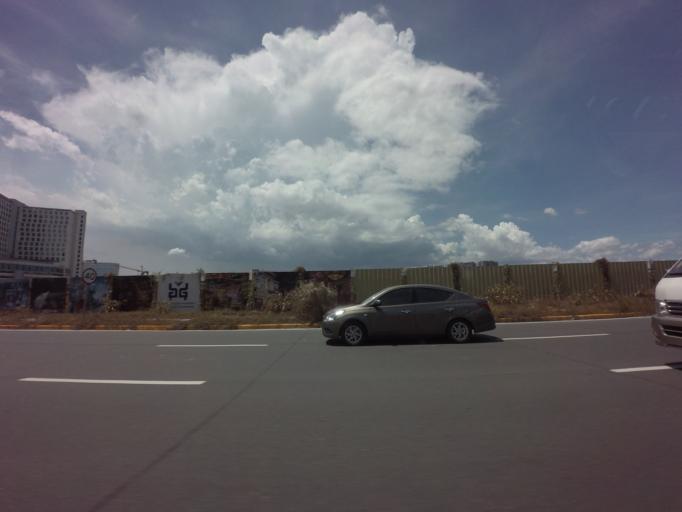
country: PH
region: Metro Manila
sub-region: Makati City
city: Makati City
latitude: 14.5159
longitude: 120.9833
